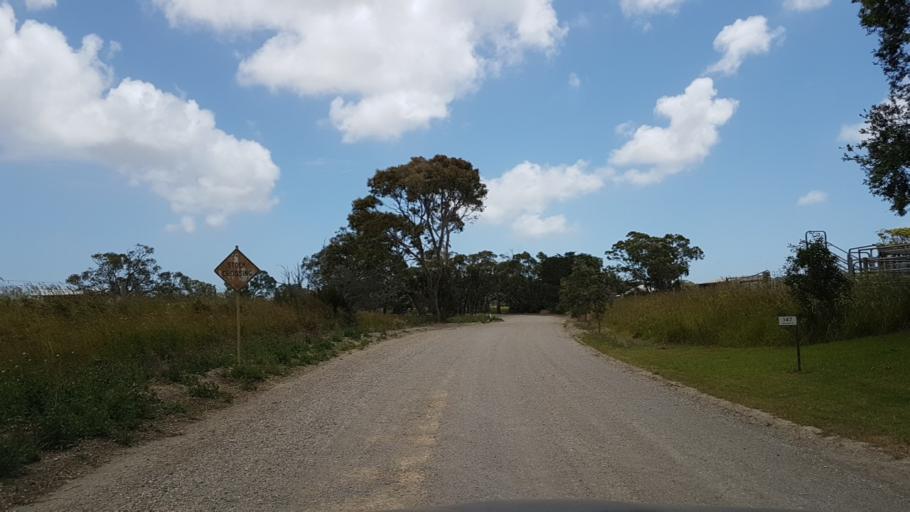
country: AU
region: South Australia
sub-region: Onkaparinga
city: Aldinga
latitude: -35.3763
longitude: 138.5009
